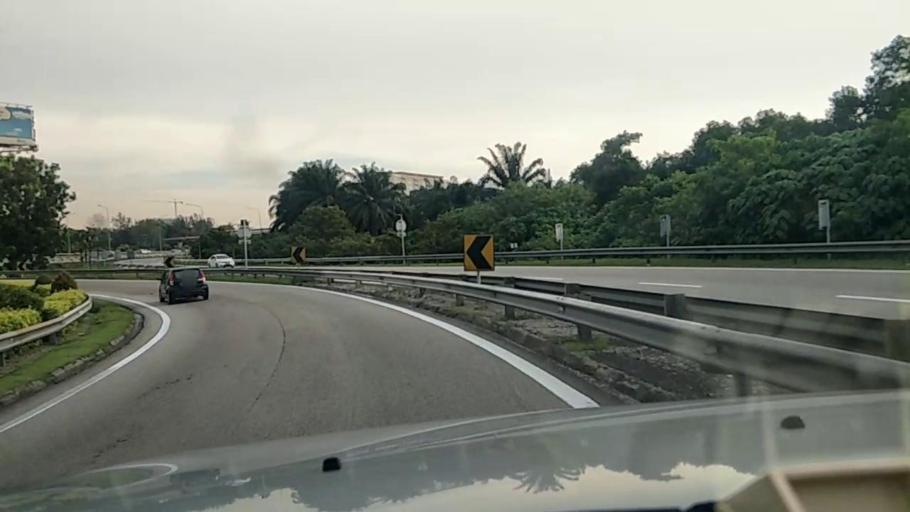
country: MY
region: Selangor
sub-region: Petaling
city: Petaling Jaya
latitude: 3.1068
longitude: 101.5885
